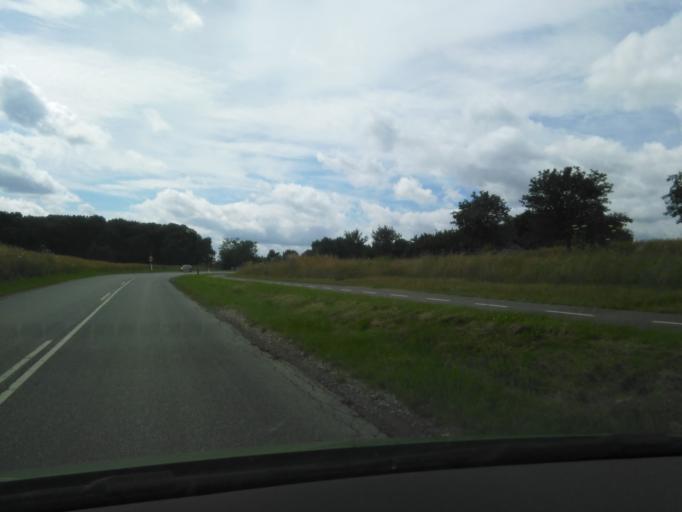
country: DK
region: Central Jutland
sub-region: Arhus Kommune
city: Logten
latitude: 56.2459
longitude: 10.3120
